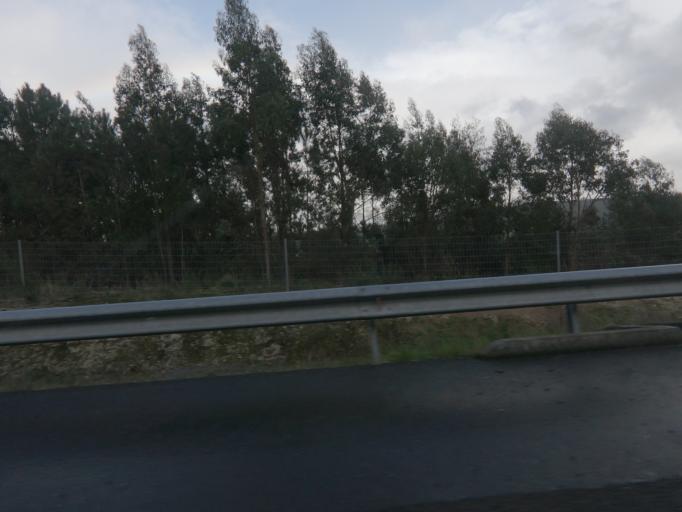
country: ES
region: Galicia
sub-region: Provincia da Coruna
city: Ribeira
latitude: 42.7357
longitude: -8.3665
